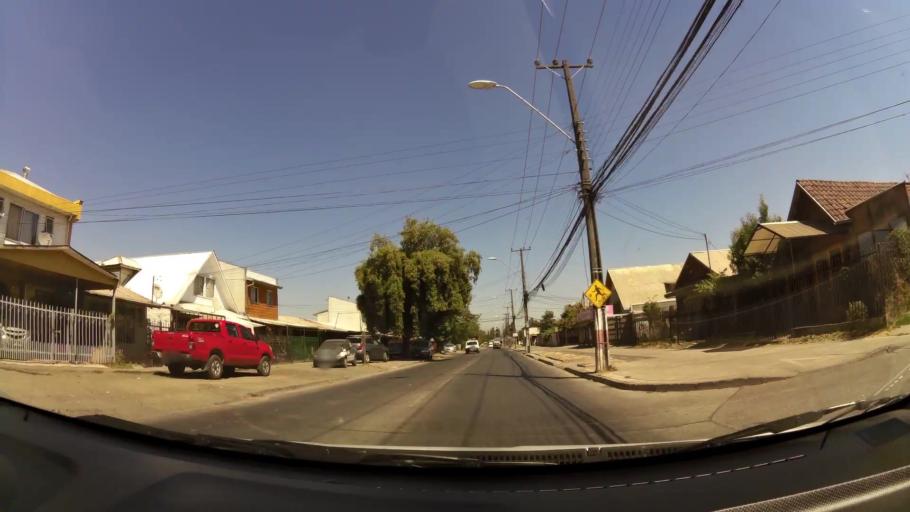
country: CL
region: Maule
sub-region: Provincia de Curico
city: Curico
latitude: -34.9695
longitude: -71.2448
